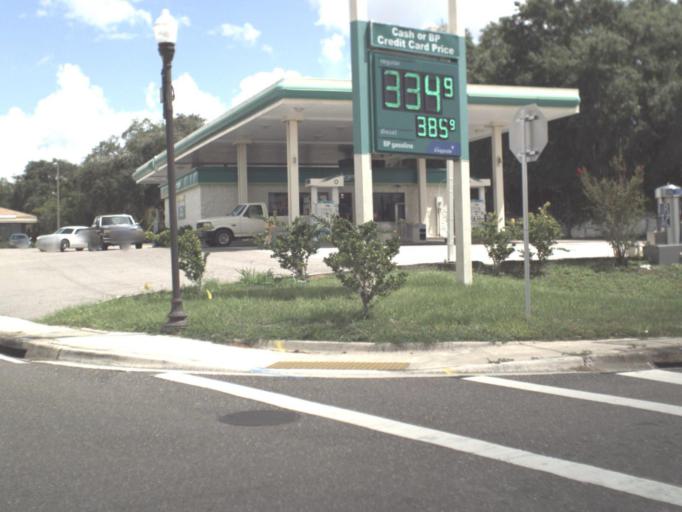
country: US
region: Florida
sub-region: Polk County
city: Haines City
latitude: 28.1055
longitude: -81.6315
